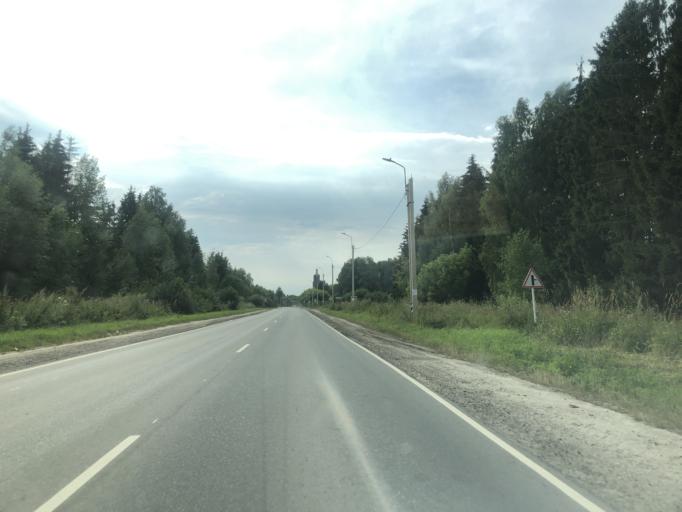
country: RU
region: Ivanovo
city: Shuya
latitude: 56.8534
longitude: 41.5586
